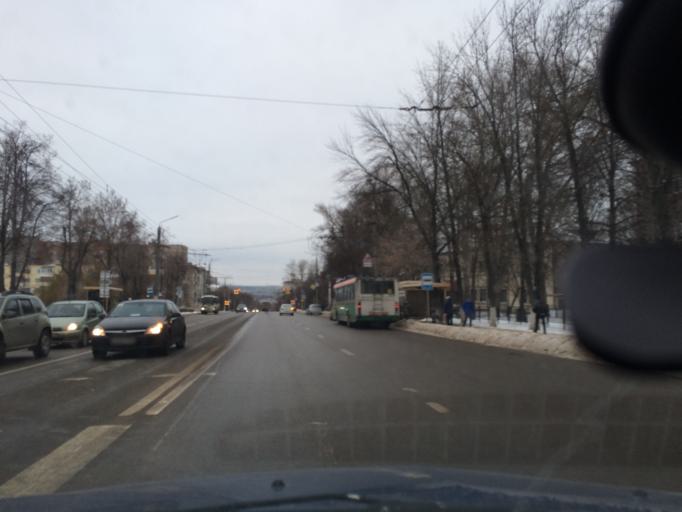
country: RU
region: Tula
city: Tula
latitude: 54.1909
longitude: 37.5839
